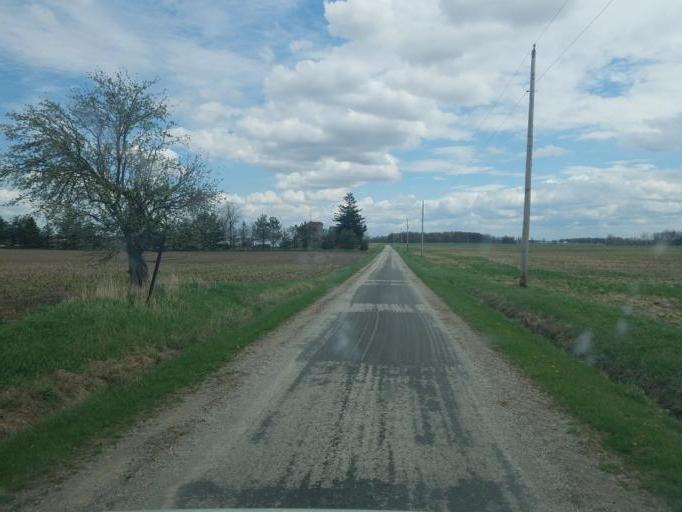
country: US
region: Ohio
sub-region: Crawford County
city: Bucyrus
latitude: 40.9143
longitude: -82.8894
